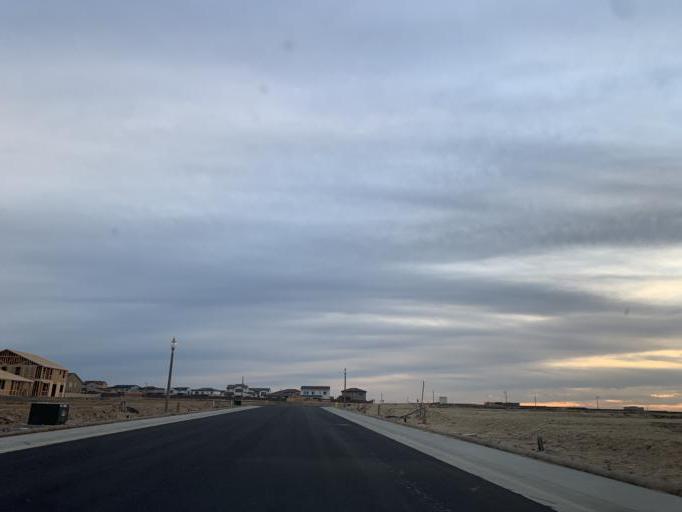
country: US
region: California
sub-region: Placer County
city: Lincoln
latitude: 38.8624
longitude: -121.2890
